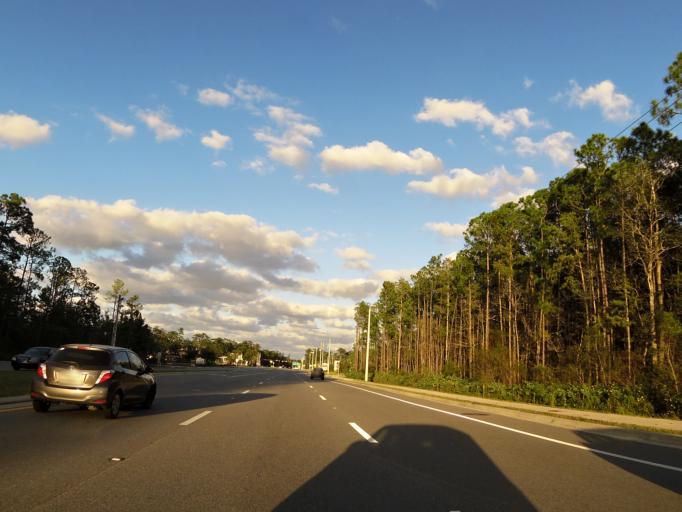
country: US
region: Florida
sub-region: Saint Johns County
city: Fruit Cove
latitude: 30.0610
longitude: -81.5086
